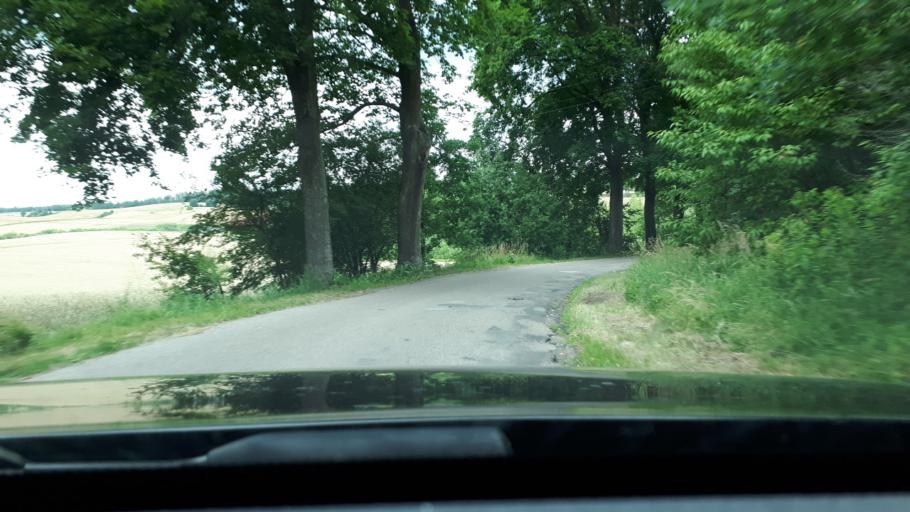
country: PL
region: Warmian-Masurian Voivodeship
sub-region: Powiat ostrodzki
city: Ostroda
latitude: 53.6817
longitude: 20.0538
